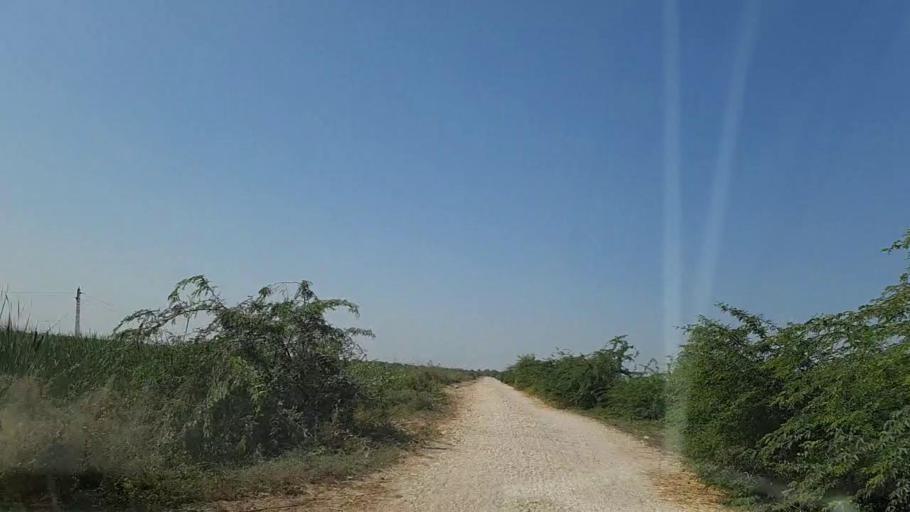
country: PK
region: Sindh
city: Chuhar Jamali
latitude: 24.4154
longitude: 68.0373
